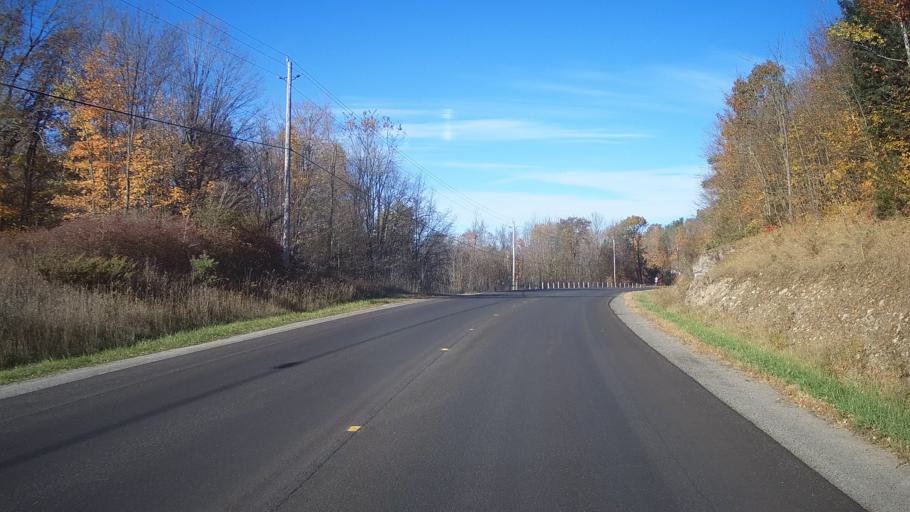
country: CA
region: Ontario
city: Kingston
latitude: 44.4743
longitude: -76.4912
